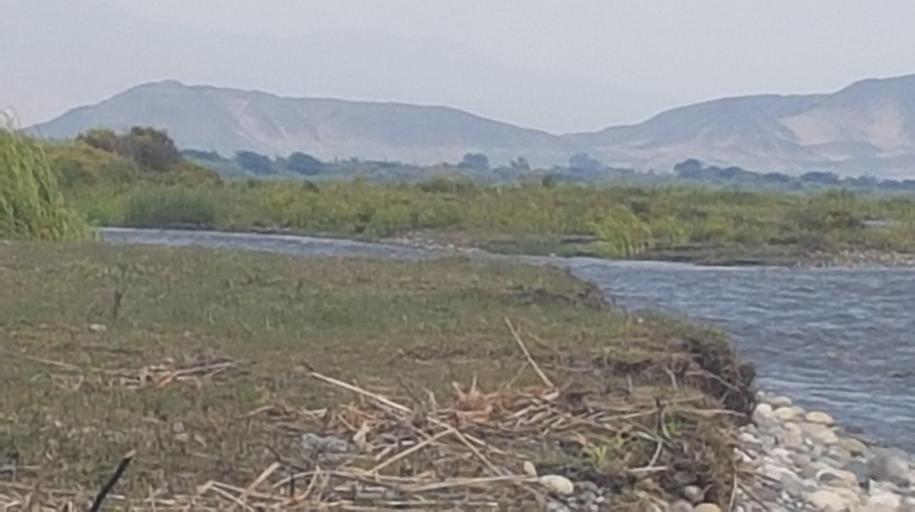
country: PE
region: Ancash
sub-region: Provincia de Santa
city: Puerto Santa
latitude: -8.9656
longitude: -78.6450
